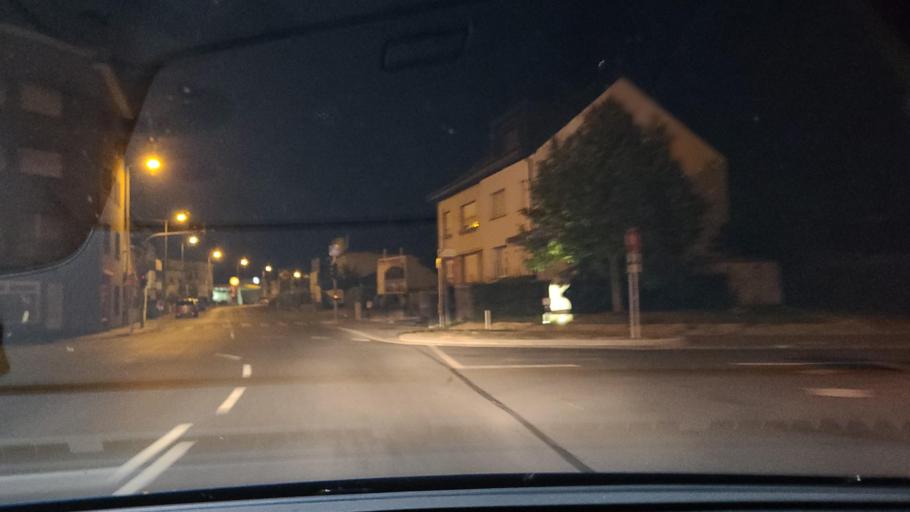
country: LU
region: Luxembourg
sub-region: Canton d'Esch-sur-Alzette
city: Obercorn
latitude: 49.5207
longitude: 5.9077
